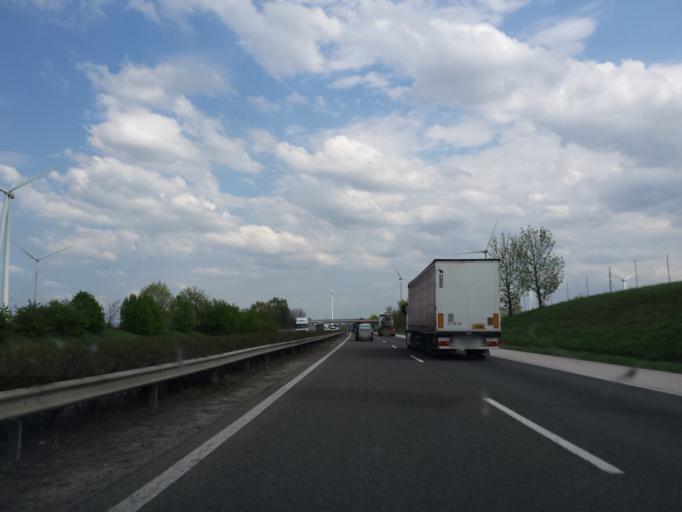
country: HU
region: Komarom-Esztergom
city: Nagyigmand
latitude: 47.6750
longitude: 18.0624
